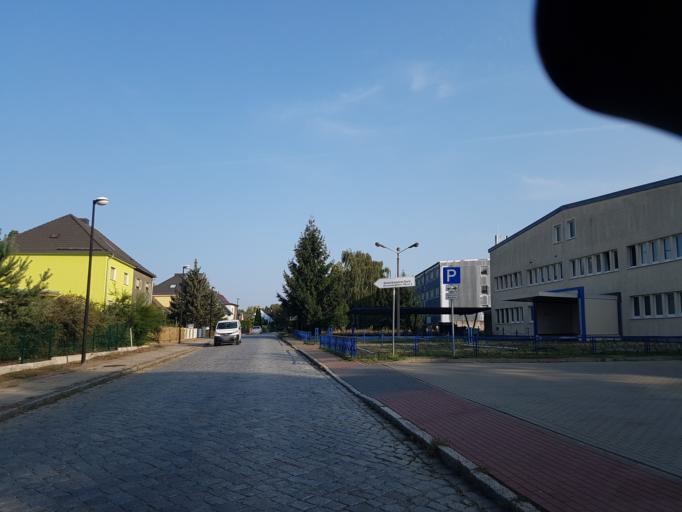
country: DE
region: Saxony-Anhalt
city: Coswig
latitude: 51.8912
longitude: 12.4411
